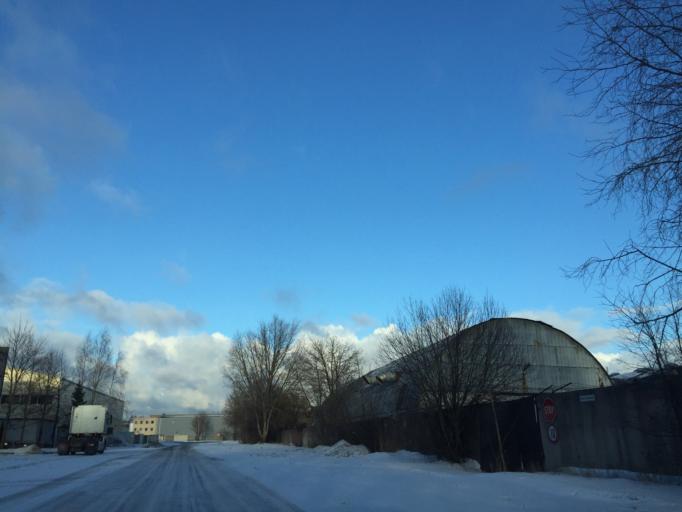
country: LV
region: Riga
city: Riga
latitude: 56.9872
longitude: 24.1118
